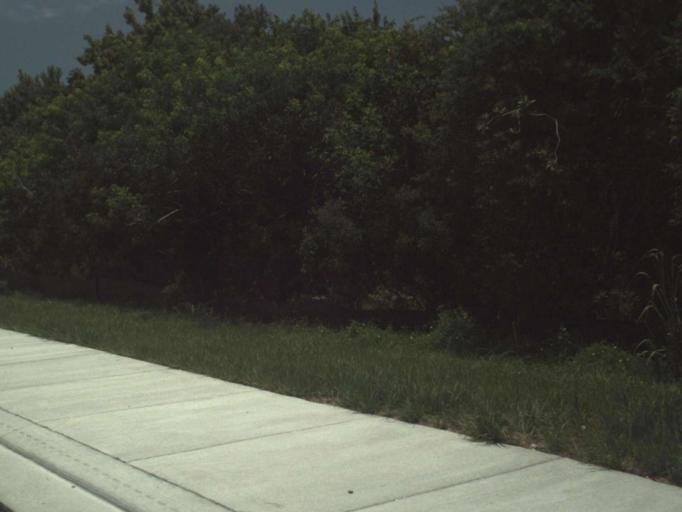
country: US
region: Florida
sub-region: Indian River County
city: Florida Ridge
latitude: 27.5702
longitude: -80.3725
